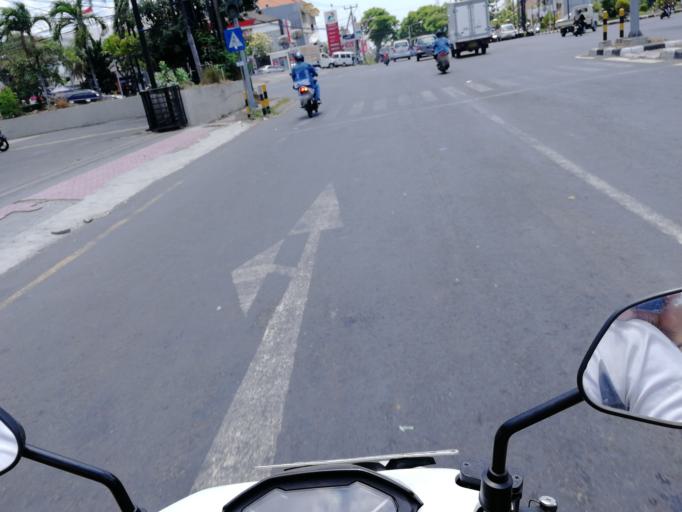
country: ID
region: Bali
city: Banjar Kertasari
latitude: -8.6367
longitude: 115.1847
